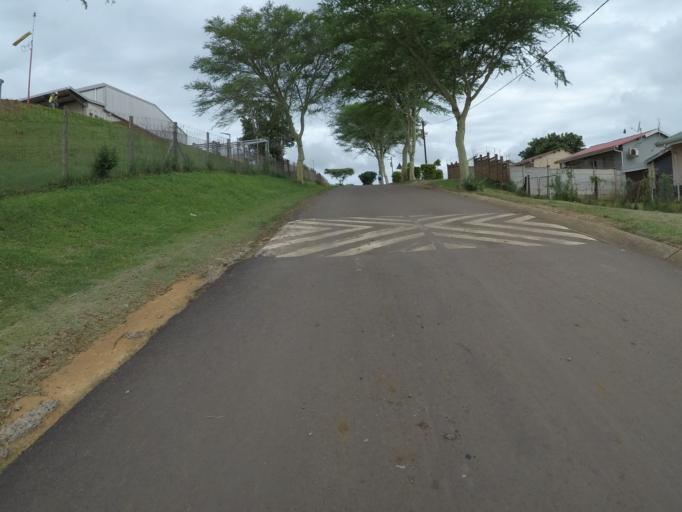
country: ZA
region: KwaZulu-Natal
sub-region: uThungulu District Municipality
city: Empangeni
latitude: -28.7799
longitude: 31.8638
